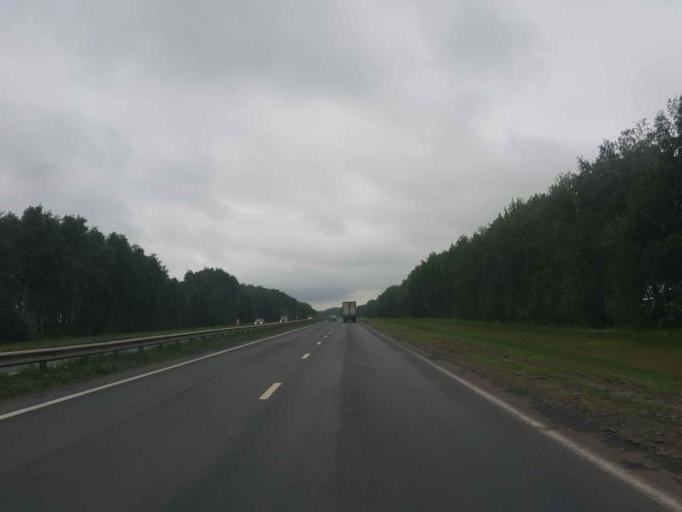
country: RU
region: Tambov
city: Selezni
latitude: 52.7632
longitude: 41.1188
